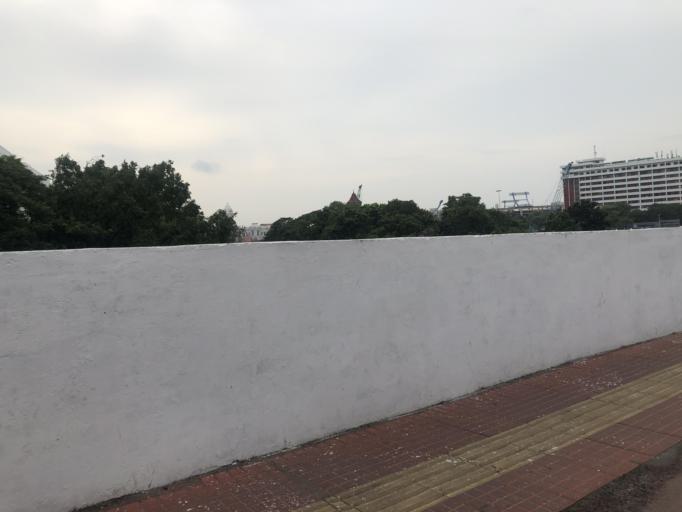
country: IN
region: Tamil Nadu
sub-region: Chennai
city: Chennai
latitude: 13.0796
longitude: 80.2753
